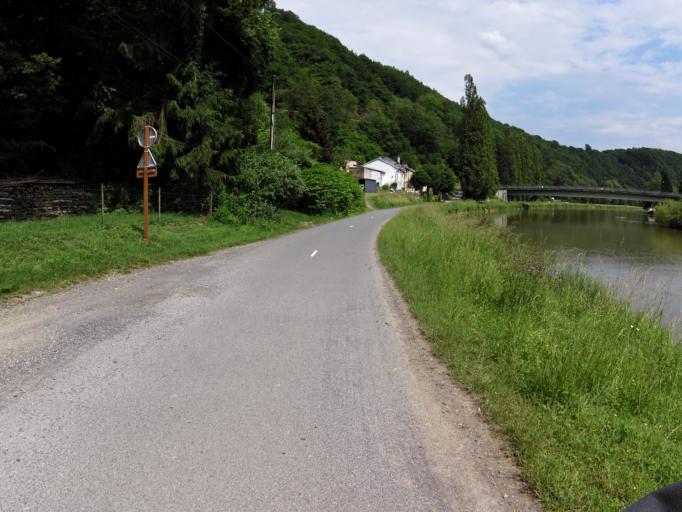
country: FR
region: Champagne-Ardenne
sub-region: Departement des Ardennes
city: Nouzonville
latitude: 49.8405
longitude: 4.7599
